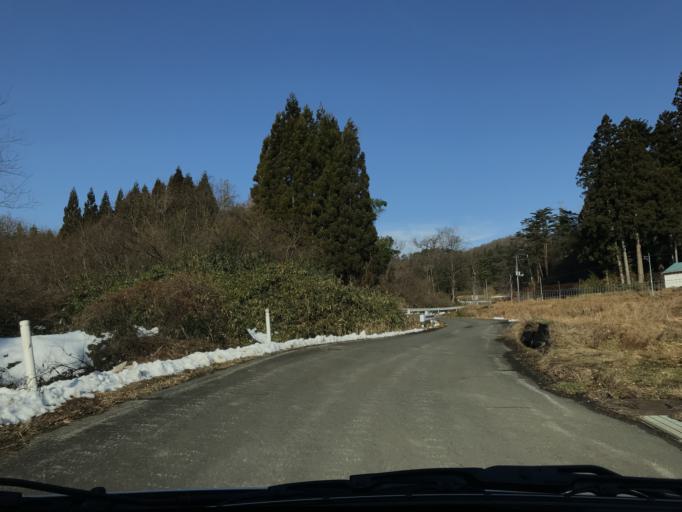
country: JP
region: Iwate
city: Ichinoseki
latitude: 38.9708
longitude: 141.0396
